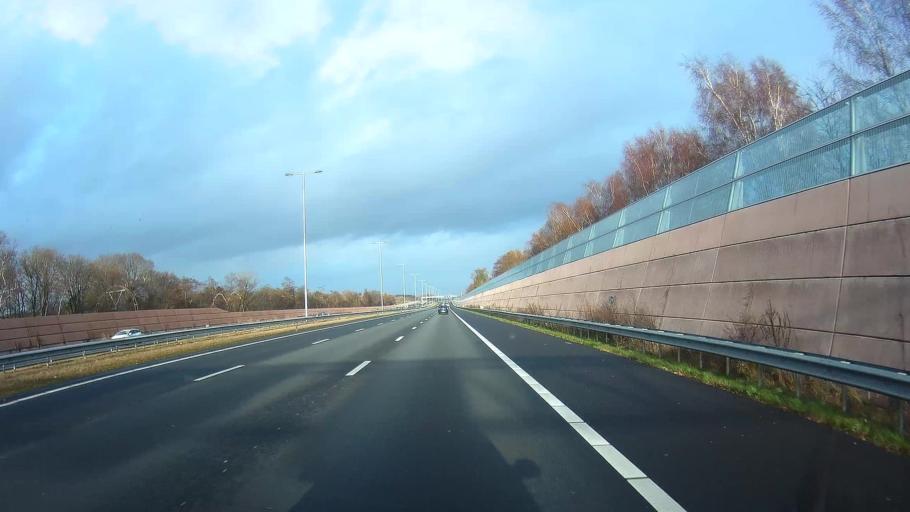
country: NL
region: North Holland
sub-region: Gemeente Wijdemeren
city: Nieuw-Loosdrecht
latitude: 52.1712
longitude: 5.1761
